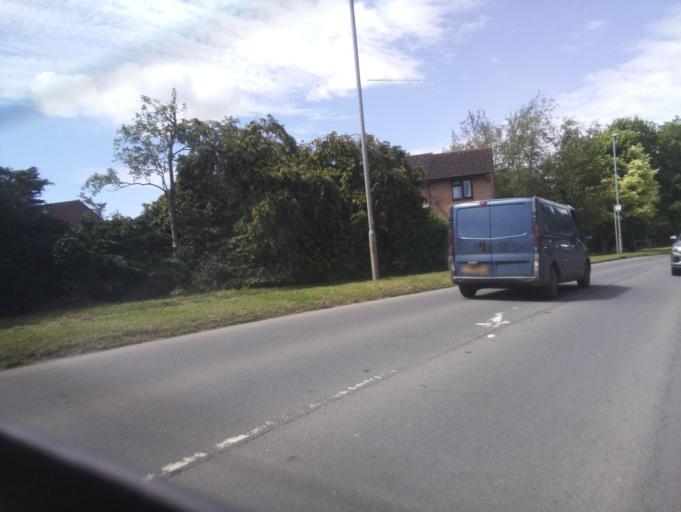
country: GB
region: England
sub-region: Devon
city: Cullompton
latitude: 50.8582
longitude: -3.3798
